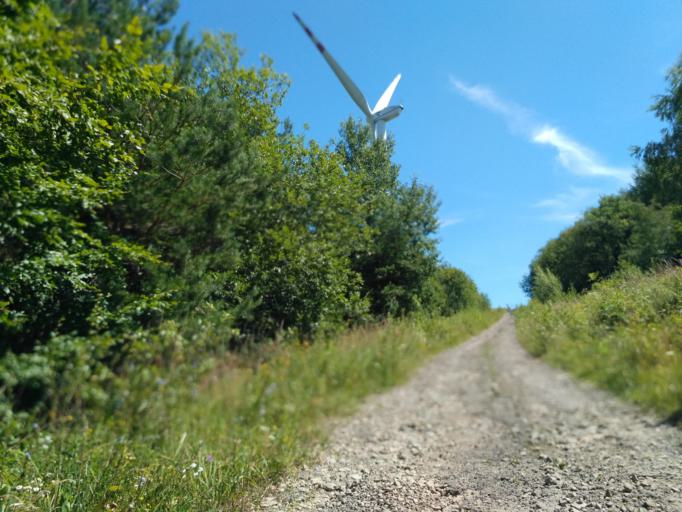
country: PL
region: Subcarpathian Voivodeship
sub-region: Powiat sanocki
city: Bukowsko
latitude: 49.4884
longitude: 22.0860
